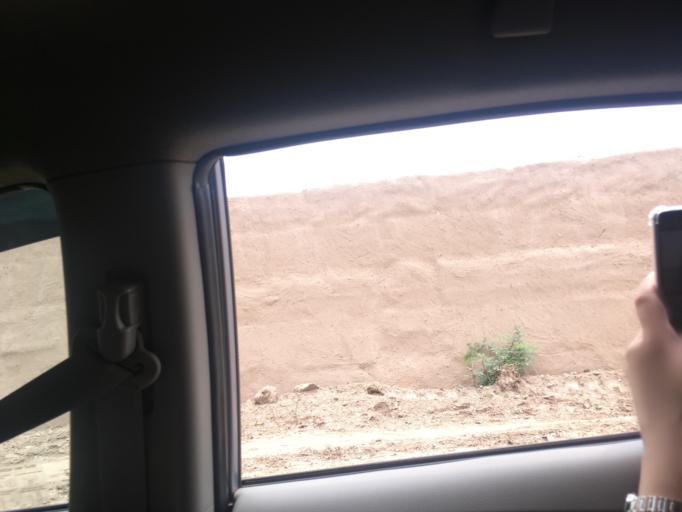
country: PK
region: Punjab
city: Lahore
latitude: 31.6238
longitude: 74.3473
